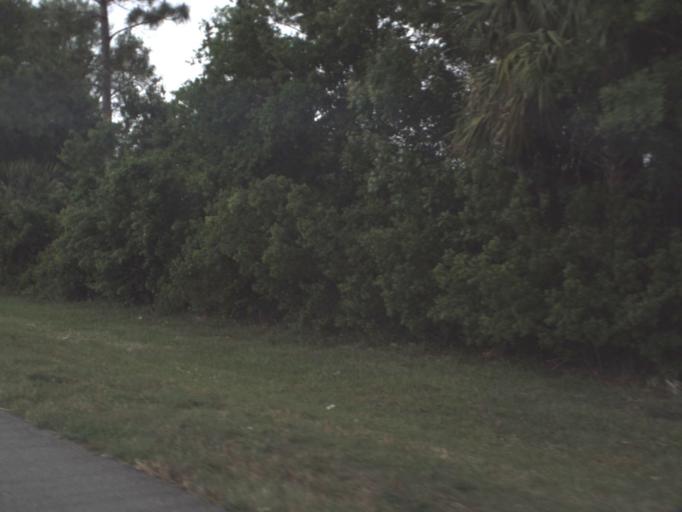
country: US
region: Florida
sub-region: Flagler County
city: Bunnell
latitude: 29.4794
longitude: -81.3405
